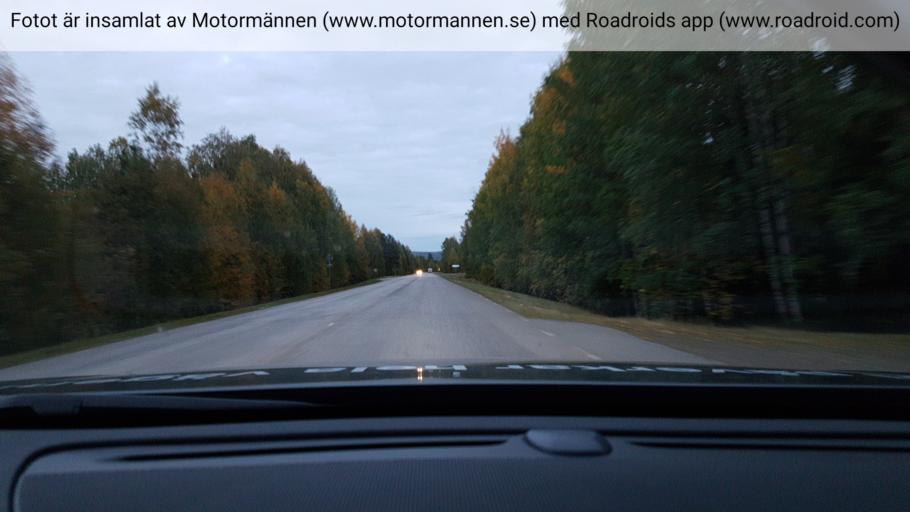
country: SE
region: Norrbotten
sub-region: Alvsbyns Kommun
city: AElvsbyn
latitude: 65.8459
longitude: 20.4770
